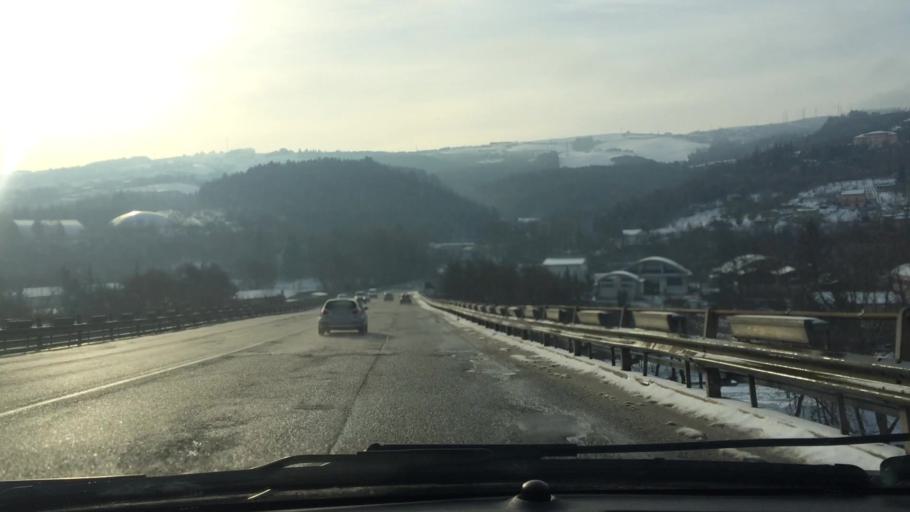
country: IT
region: Basilicate
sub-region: Provincia di Potenza
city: Potenza
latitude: 40.6280
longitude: 15.8055
